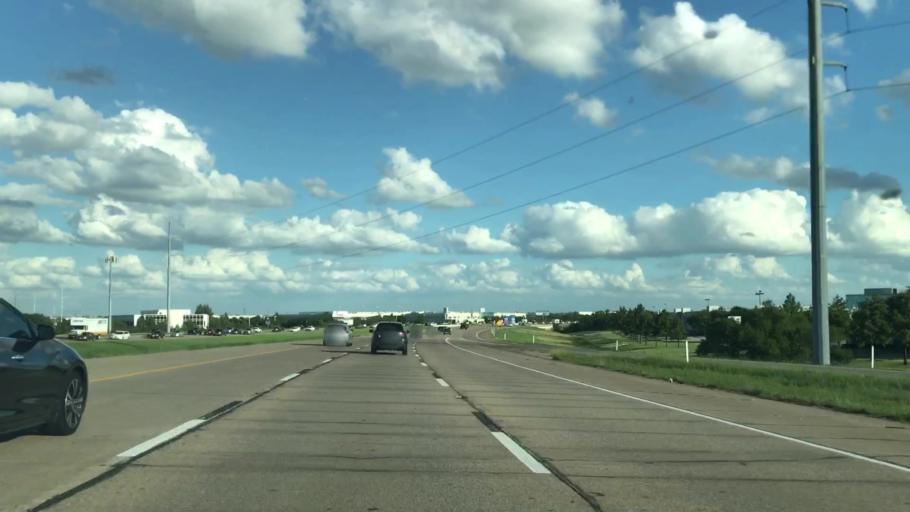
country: US
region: Texas
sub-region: Dallas County
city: Coppell
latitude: 32.9441
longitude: -97.0193
